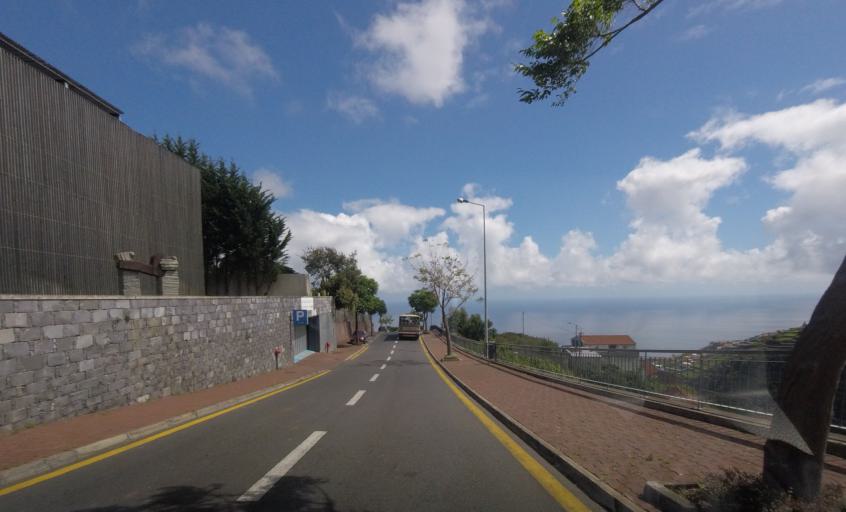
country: PT
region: Madeira
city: Camara de Lobos
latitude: 32.6705
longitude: -16.9803
